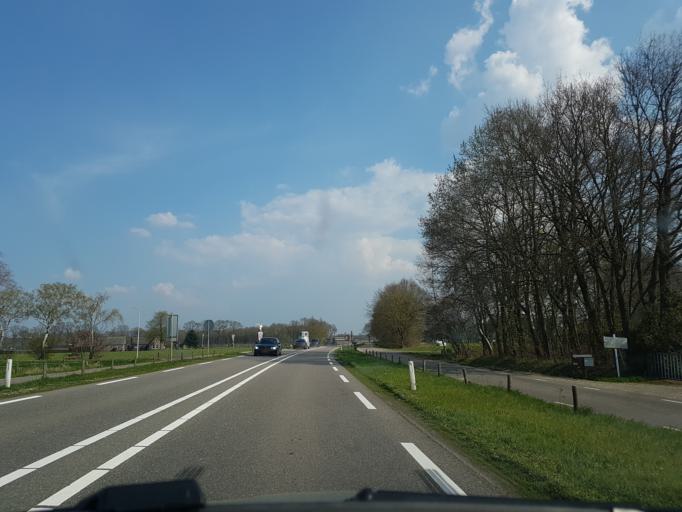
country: NL
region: Overijssel
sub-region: Gemeente Dalfsen
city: Dalfsen
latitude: 52.5303
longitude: 6.3206
